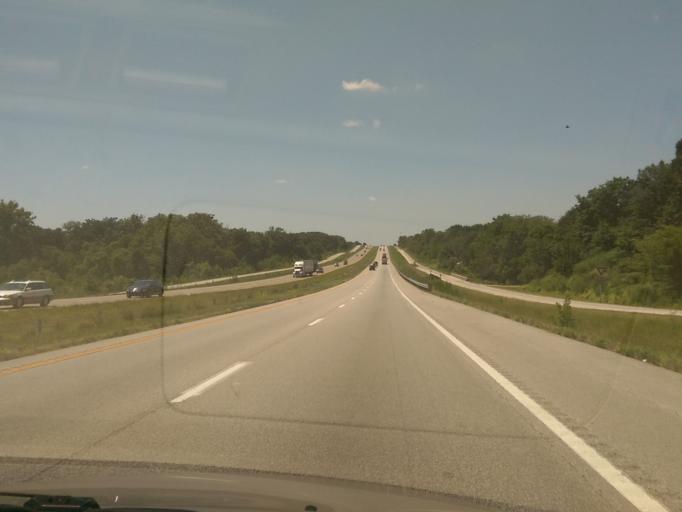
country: US
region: Missouri
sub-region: Cooper County
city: Boonville
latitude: 38.9353
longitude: -92.8728
